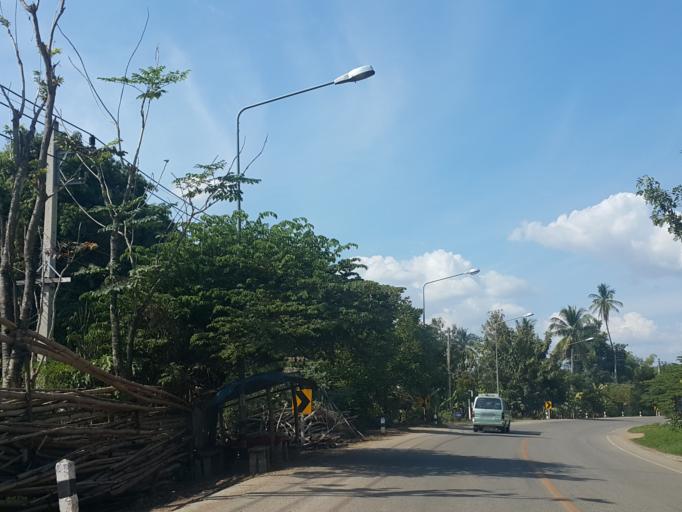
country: TH
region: Sukhothai
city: Sawankhalok
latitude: 17.2956
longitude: 99.8273
